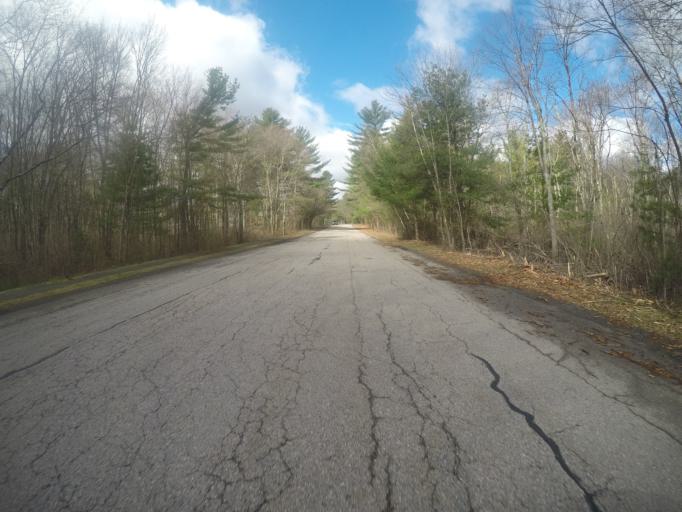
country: US
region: Massachusetts
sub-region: Bristol County
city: Easton
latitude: 42.0417
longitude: -71.1280
